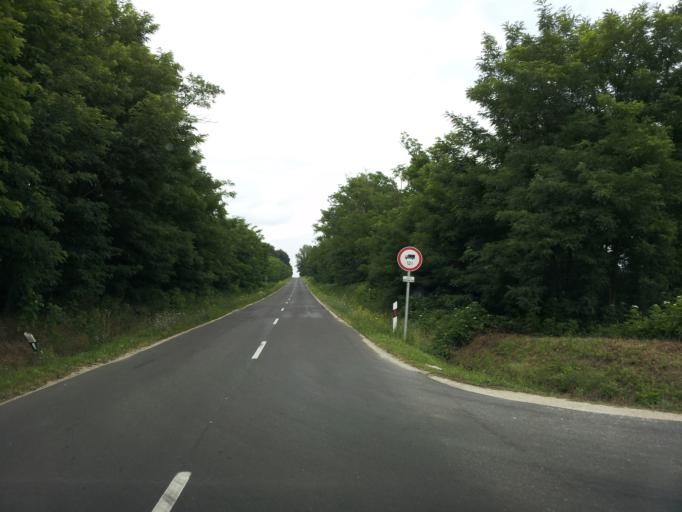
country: HU
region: Zala
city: Turje
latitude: 47.0413
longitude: 16.9901
